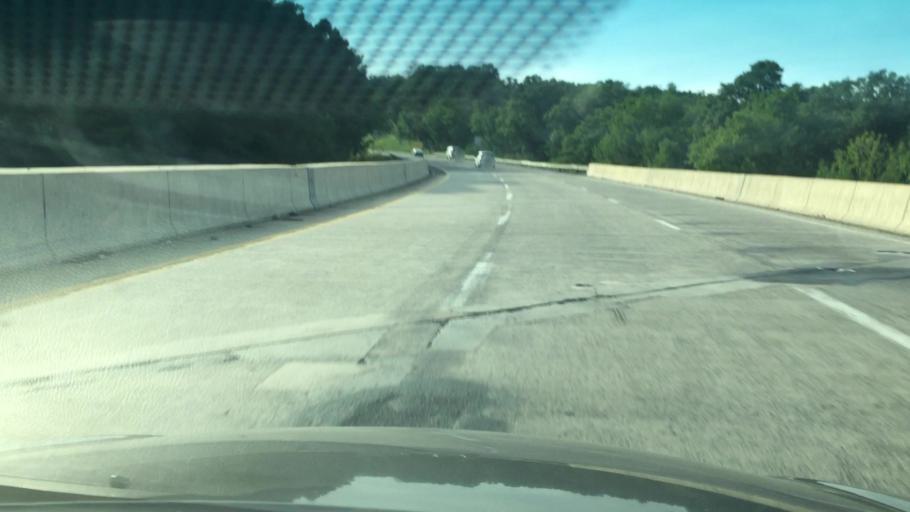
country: US
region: Pennsylvania
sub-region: Monroe County
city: Tannersville
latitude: 41.0545
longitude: -75.3175
